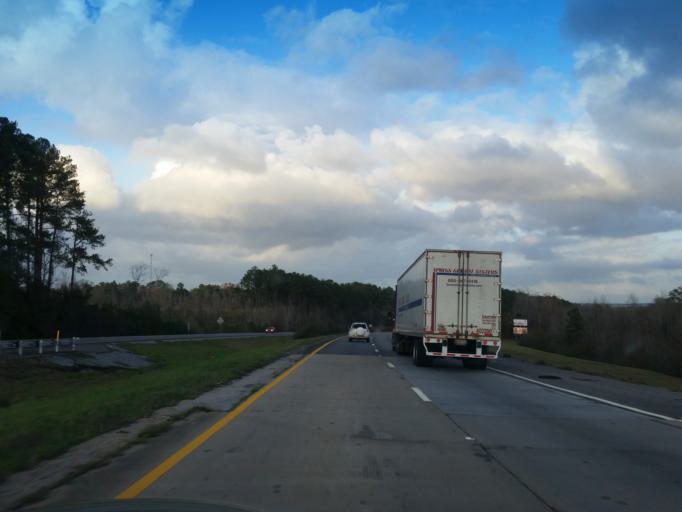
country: US
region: Mississippi
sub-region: Jones County
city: Sharon
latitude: 31.8986
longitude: -89.0279
